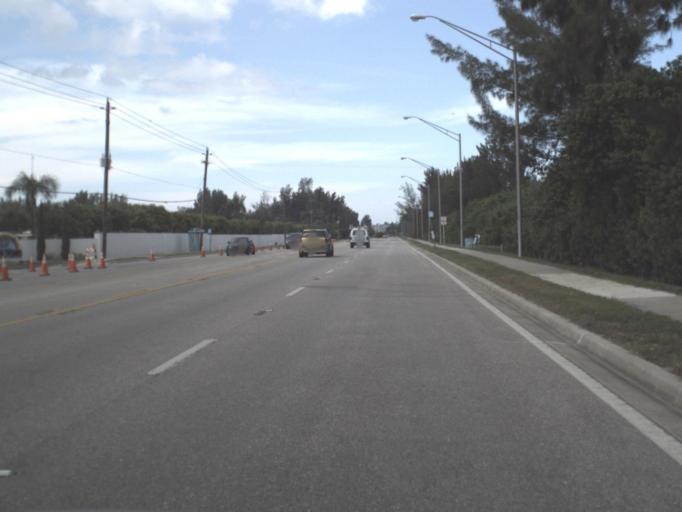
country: US
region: Florida
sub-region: Manatee County
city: Cortez
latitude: 27.4636
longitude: -82.6689
